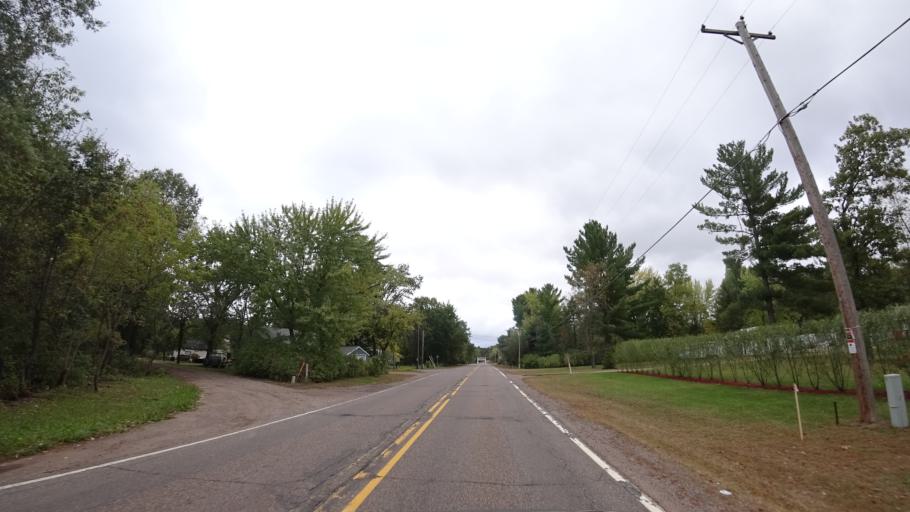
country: US
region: Wisconsin
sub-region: Chippewa County
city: Lake Wissota
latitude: 44.9496
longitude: -91.2642
